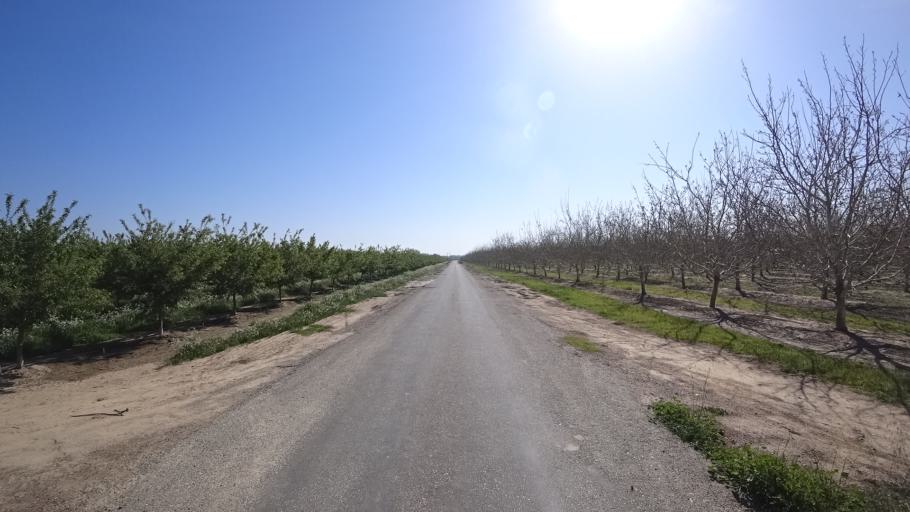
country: US
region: California
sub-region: Glenn County
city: Hamilton City
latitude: 39.6379
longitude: -122.0227
